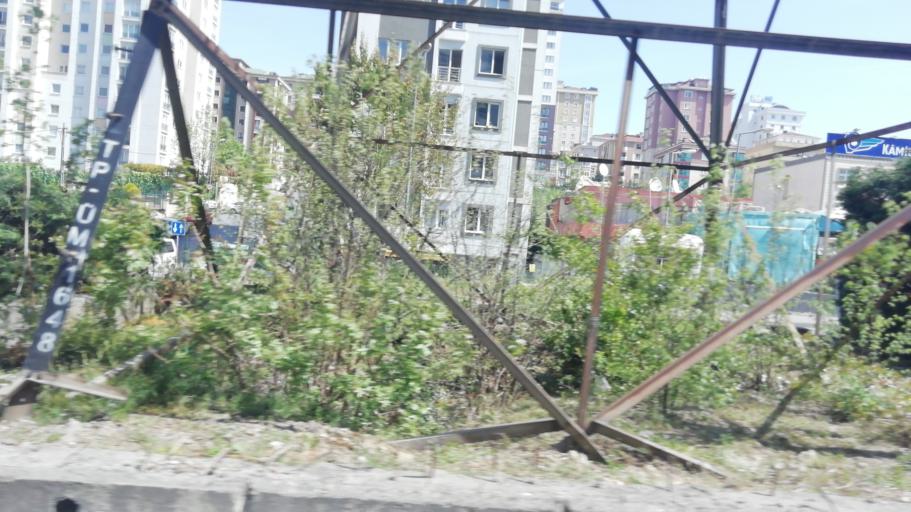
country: TR
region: Istanbul
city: Umraniye
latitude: 41.0004
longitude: 29.1459
